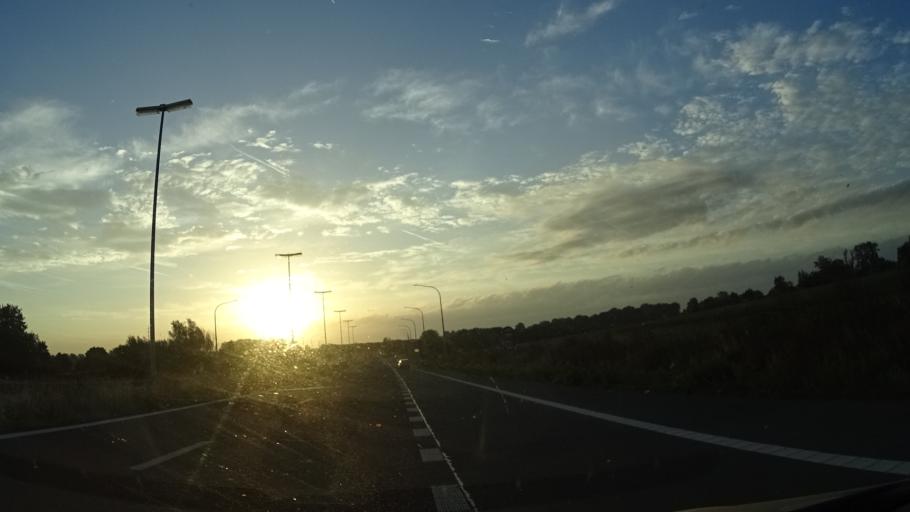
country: BE
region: Wallonia
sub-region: Province du Hainaut
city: Chasse Royale
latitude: 50.4066
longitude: 3.9536
